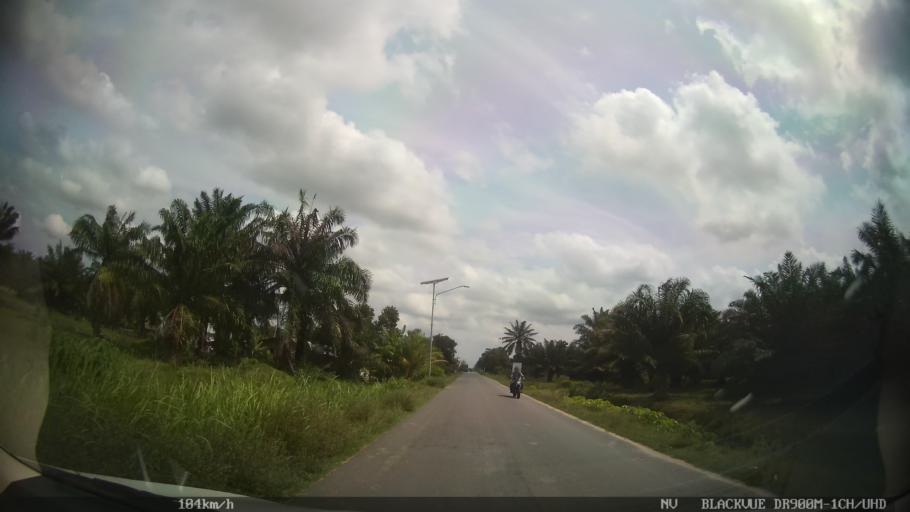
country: ID
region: North Sumatra
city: Percut
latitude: 3.5954
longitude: 98.8396
